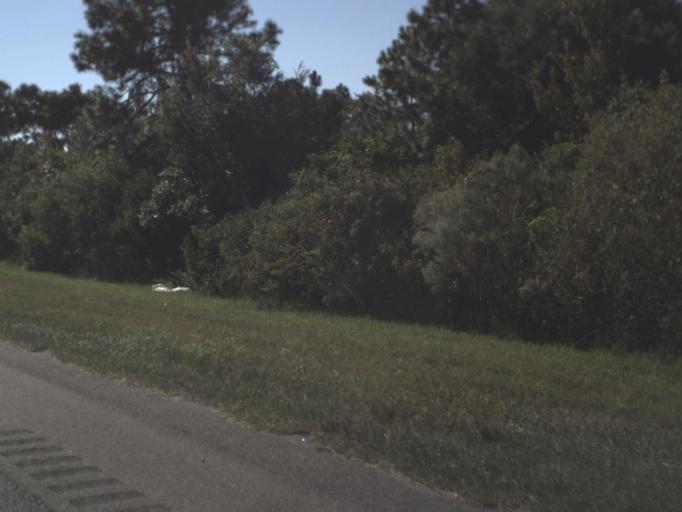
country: US
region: Florida
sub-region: Orange County
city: Williamsburg
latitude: 28.4248
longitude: -81.4192
